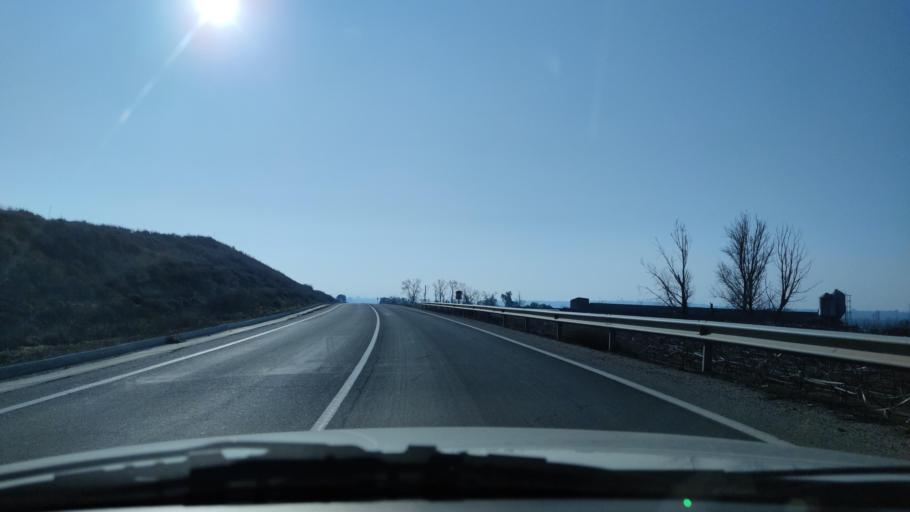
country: ES
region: Catalonia
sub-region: Provincia de Lleida
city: Albesa
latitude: 41.7318
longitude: 0.6395
